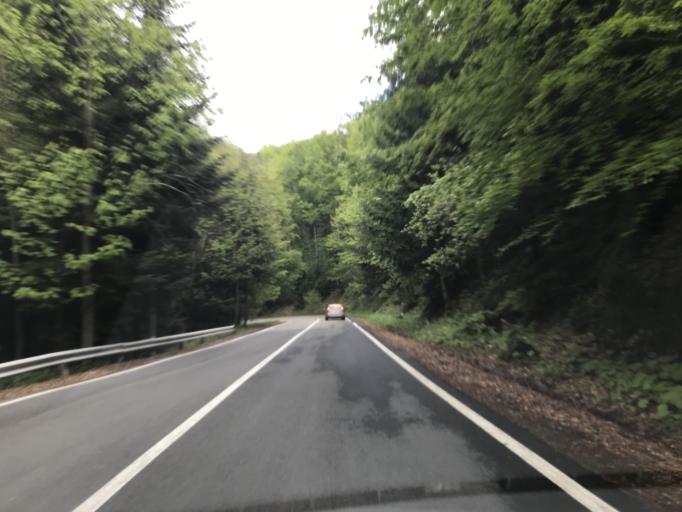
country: RO
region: Sibiu
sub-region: Comuna Cartisoara
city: Cartisoara
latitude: 45.6725
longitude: 24.5886
